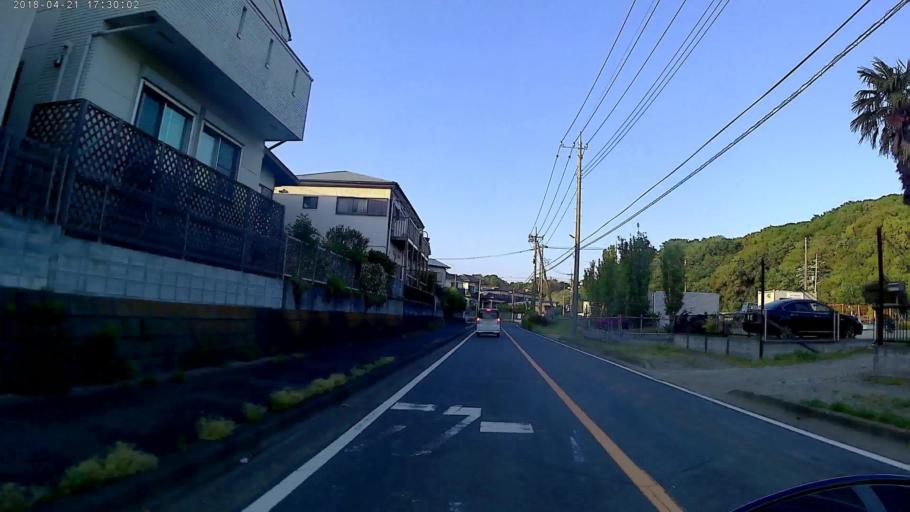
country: JP
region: Kanagawa
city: Atsugi
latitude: 35.4304
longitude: 139.4175
